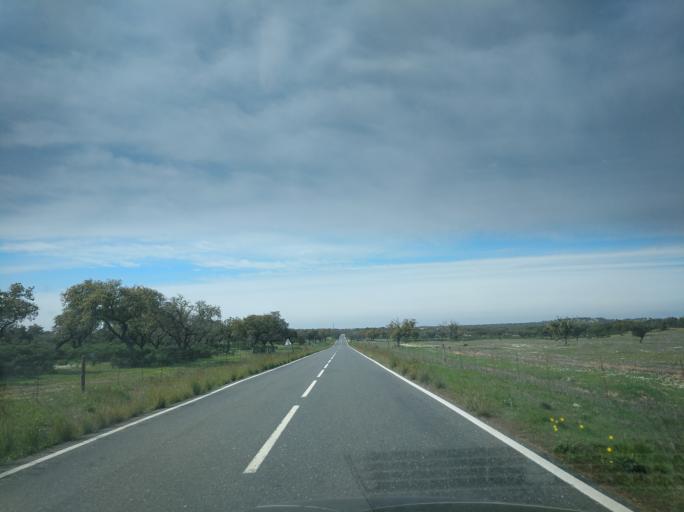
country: PT
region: Beja
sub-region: Mertola
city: Mertola
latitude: 37.7371
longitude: -7.7748
